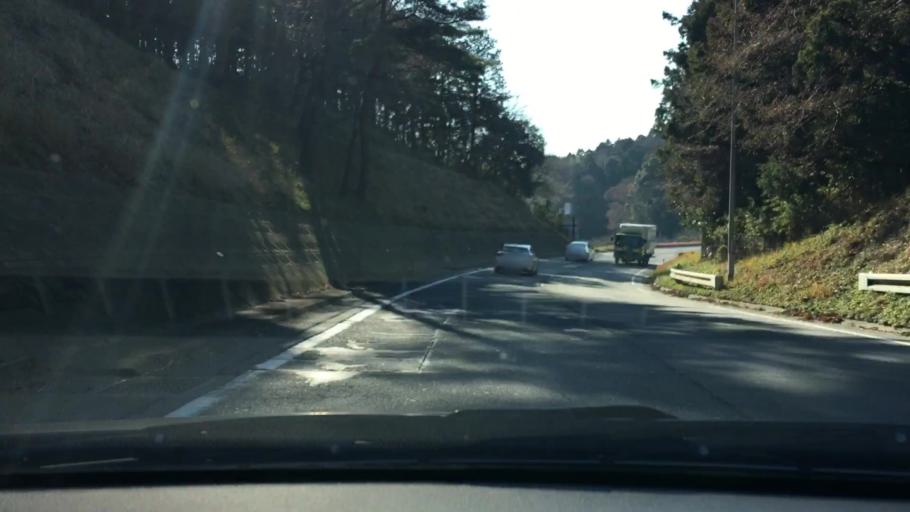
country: JP
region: Chiba
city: Sakura
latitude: 35.6857
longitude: 140.2401
